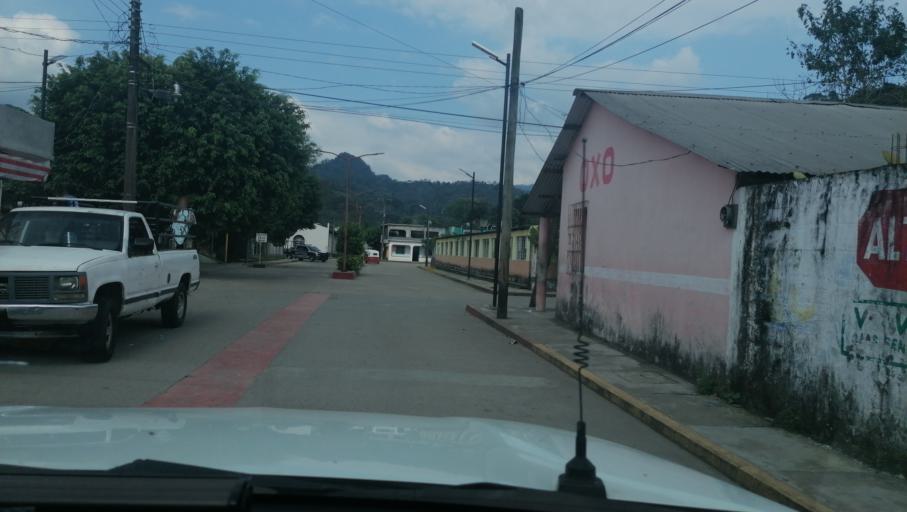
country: MX
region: Chiapas
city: Ostuacan
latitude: 17.4083
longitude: -93.3363
